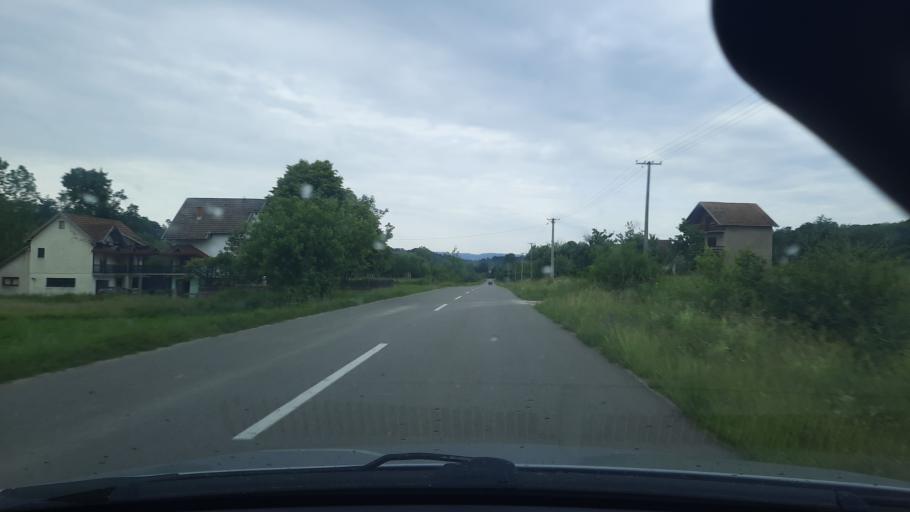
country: RS
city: Jarebice
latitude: 44.4936
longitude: 19.4864
